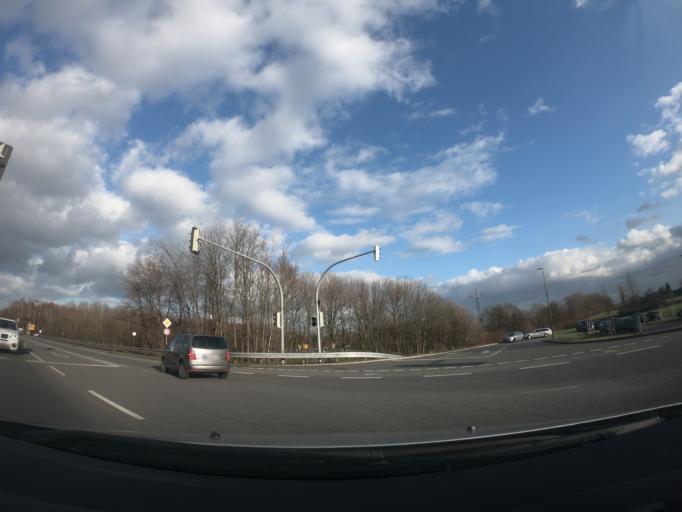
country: DE
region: North Rhine-Westphalia
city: Lunen
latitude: 51.5648
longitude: 7.5027
